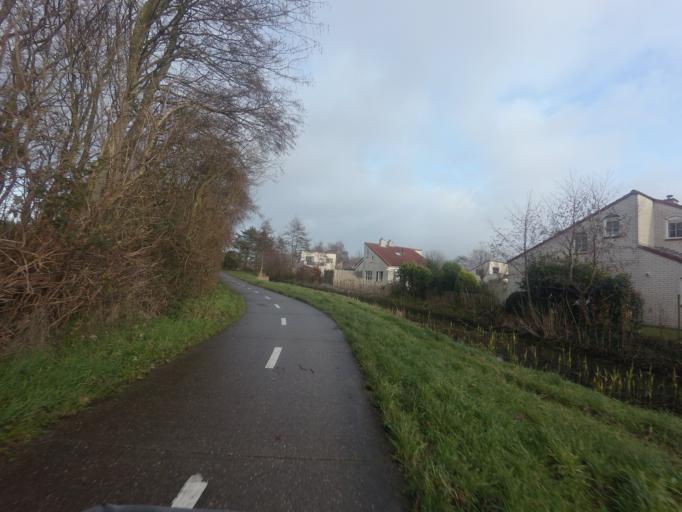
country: NL
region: North Holland
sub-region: Gemeente Texel
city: Den Burg
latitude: 53.1553
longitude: 4.8499
